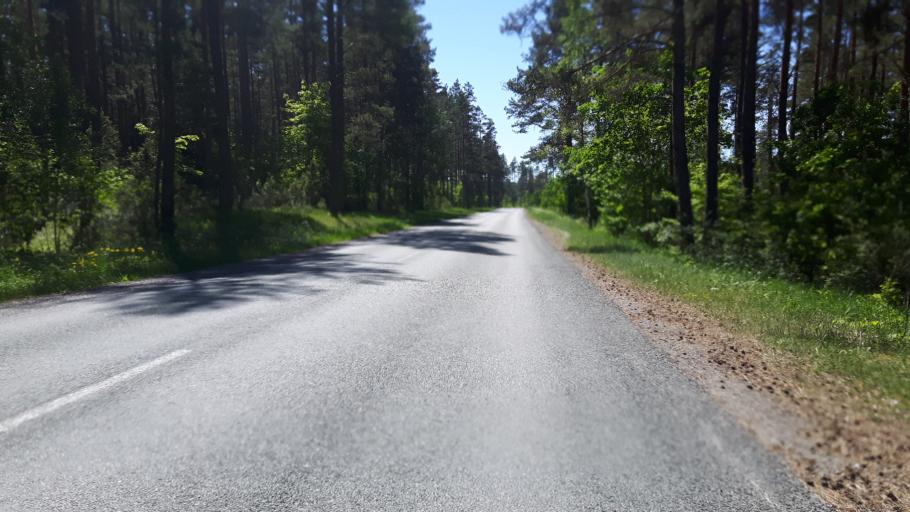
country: EE
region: Harju
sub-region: Kuusalu vald
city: Kuusalu
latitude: 59.4828
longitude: 25.4711
